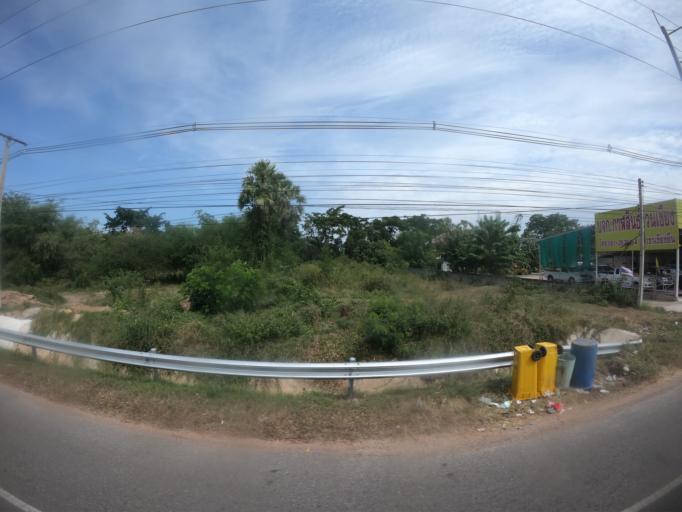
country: TH
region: Maha Sarakham
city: Chiang Yuen
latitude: 16.4145
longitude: 103.0863
